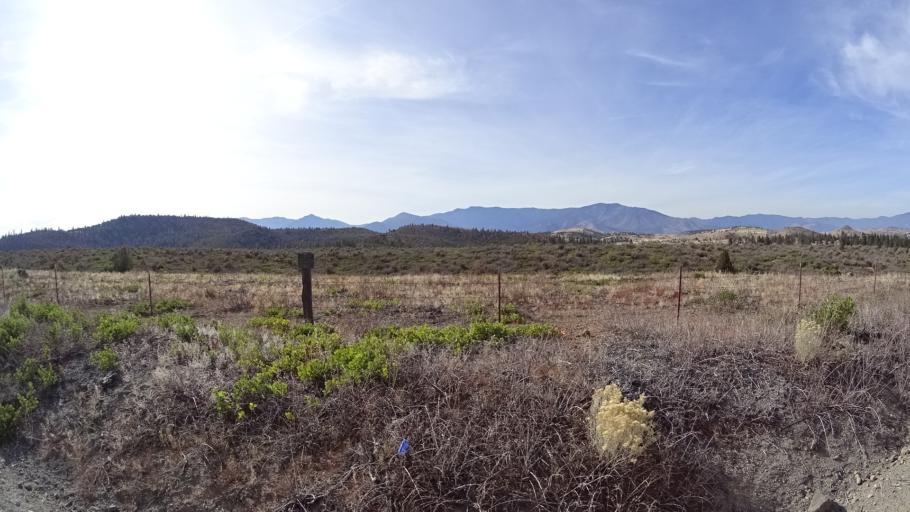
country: US
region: California
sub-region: Siskiyou County
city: Weed
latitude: 41.4851
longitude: -122.3665
